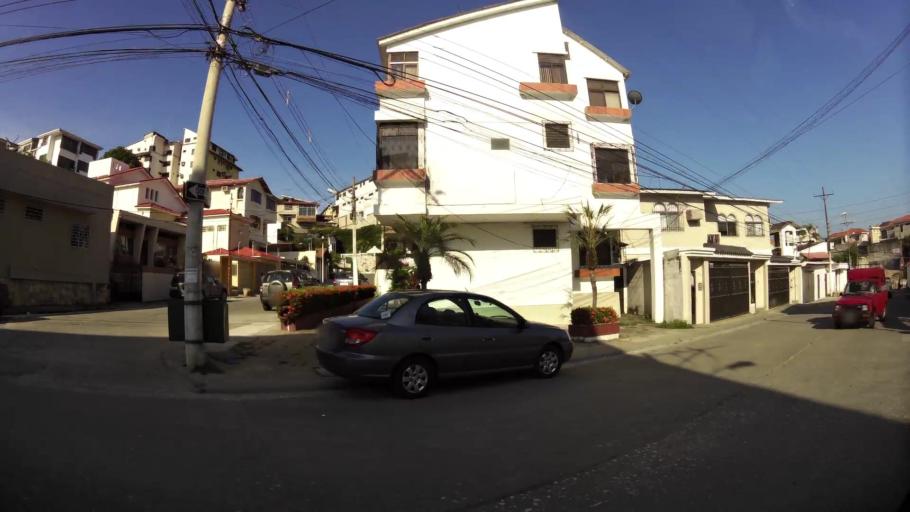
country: EC
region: Guayas
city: Guayaquil
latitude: -2.1618
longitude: -79.9077
